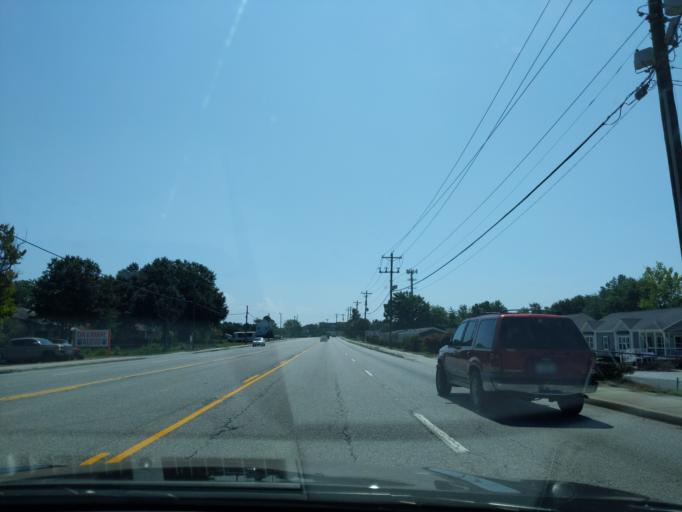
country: US
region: South Carolina
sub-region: Lexington County
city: Oak Grove
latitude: 33.9724
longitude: -81.1492
